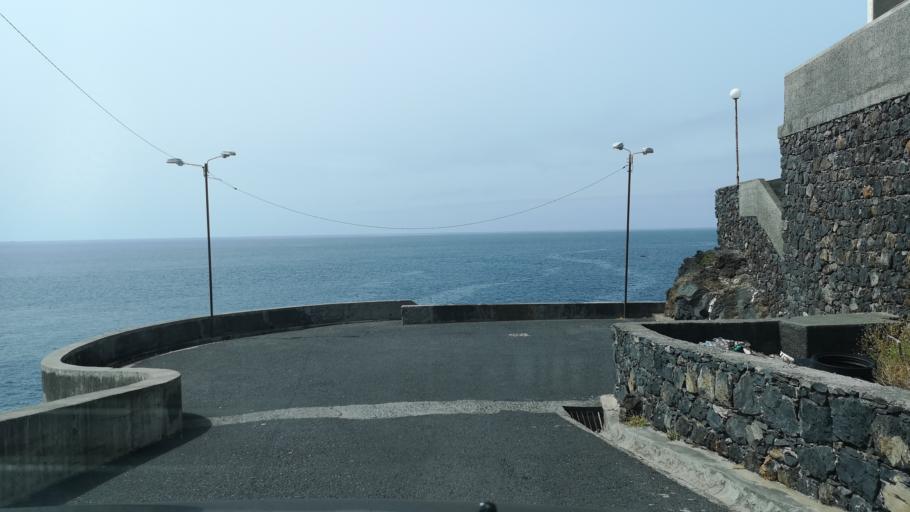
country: PT
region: Madeira
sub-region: Santa Cruz
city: Santa Cruz
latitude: 32.6632
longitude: -16.8036
